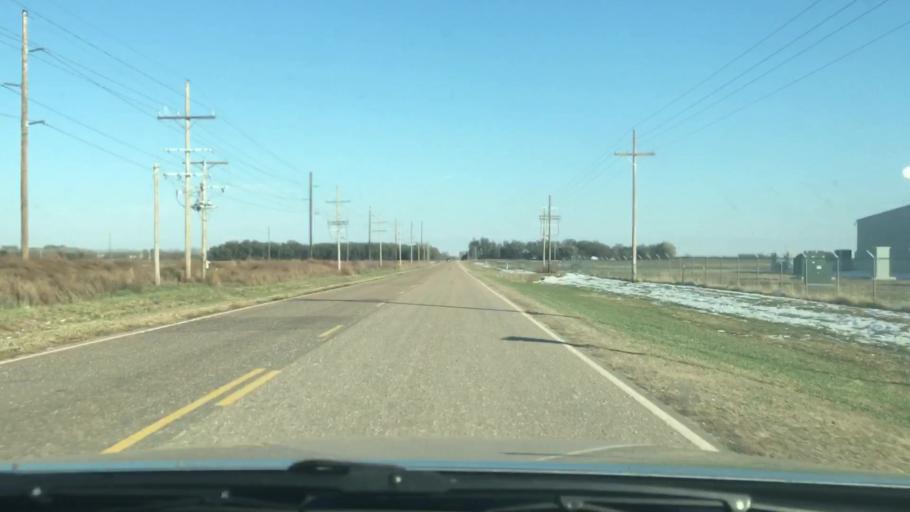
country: US
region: Kansas
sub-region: Rice County
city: Lyons
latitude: 38.2894
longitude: -98.1901
